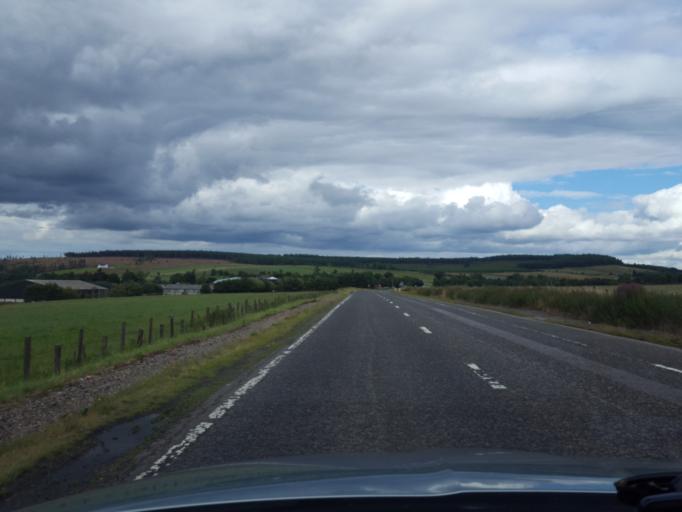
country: GB
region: Scotland
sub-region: Moray
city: Rothes
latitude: 57.4233
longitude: -3.3527
